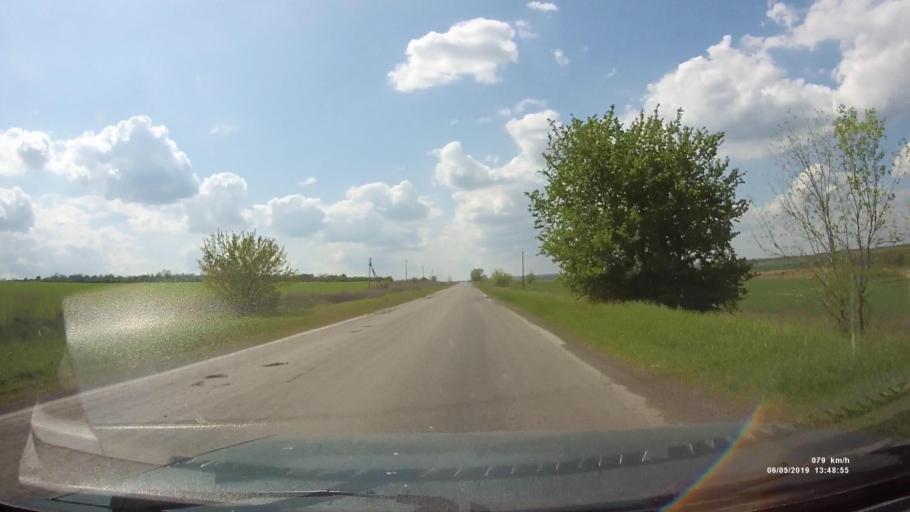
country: RU
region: Rostov
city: Melikhovskaya
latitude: 47.6590
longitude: 40.5342
